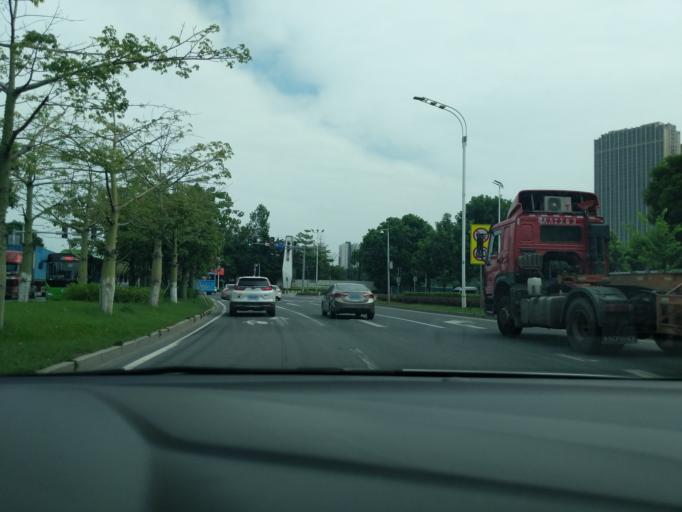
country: CN
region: Guangdong
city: Nansha
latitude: 22.7512
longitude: 113.5791
